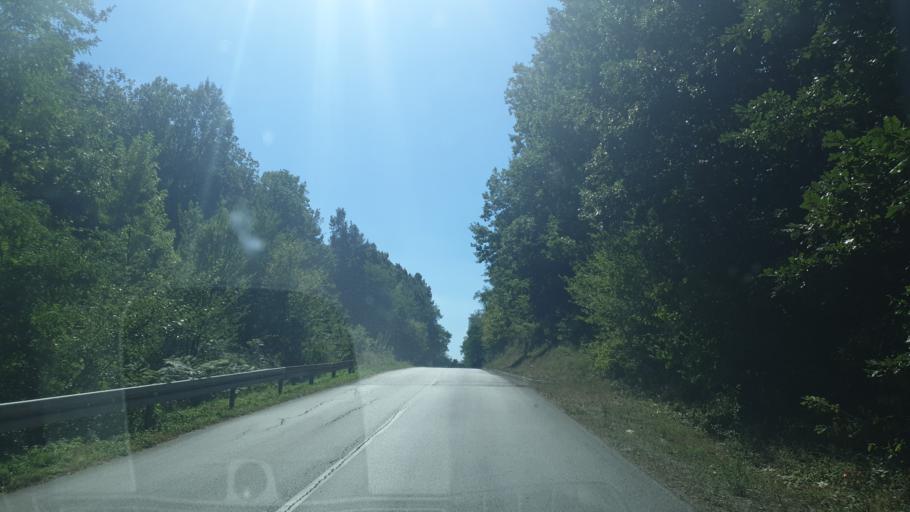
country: RS
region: Central Serbia
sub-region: Kolubarski Okrug
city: Mionica
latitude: 44.2062
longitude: 20.0806
